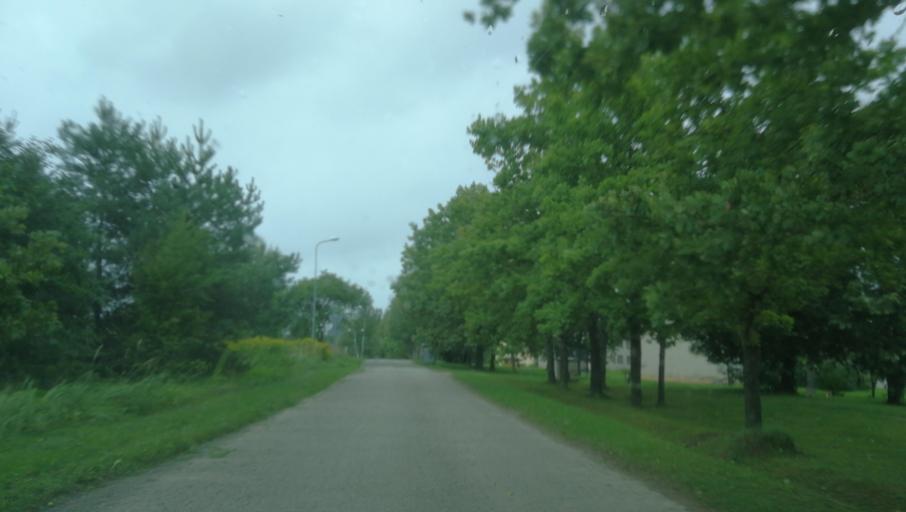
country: LV
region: Beverina
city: Murmuiza
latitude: 57.3998
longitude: 25.4722
